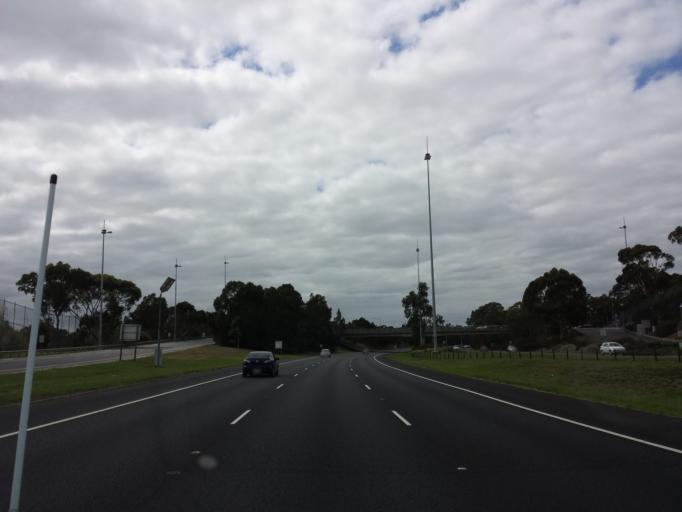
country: AU
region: Victoria
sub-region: Manningham
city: Bulleen
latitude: -37.7811
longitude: 145.0759
